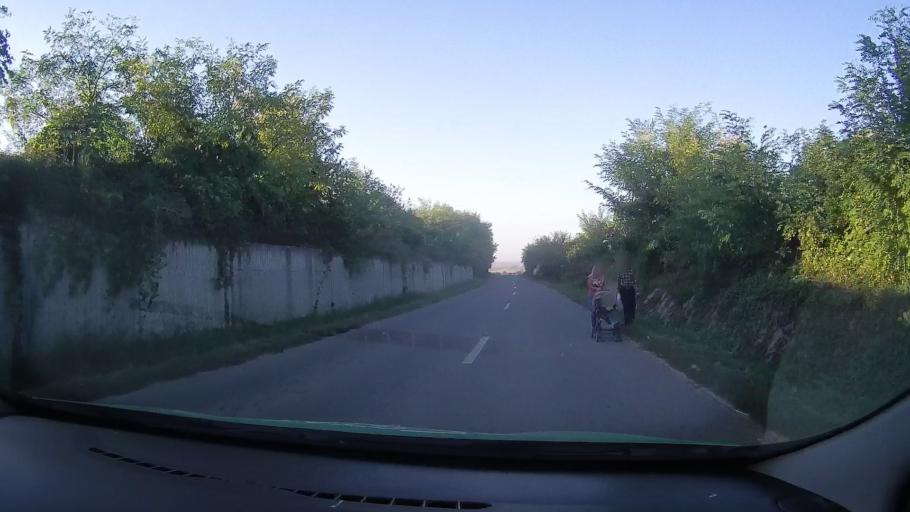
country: RO
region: Bihor
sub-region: Comuna Cetariu
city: Cetariu
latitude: 47.1485
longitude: 21.9948
